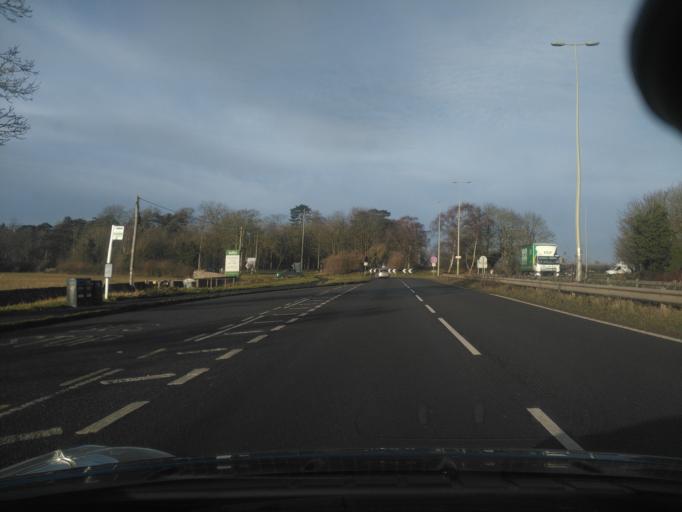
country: GB
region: England
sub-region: Oxfordshire
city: Woodstock
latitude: 51.8371
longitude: -1.3346
